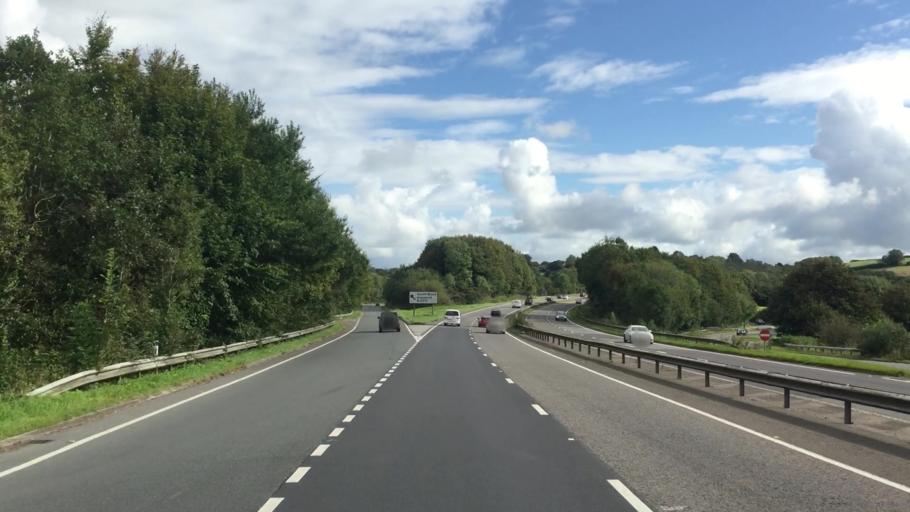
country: GB
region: England
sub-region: Devon
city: South Brent
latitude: 50.4153
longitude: -3.8420
